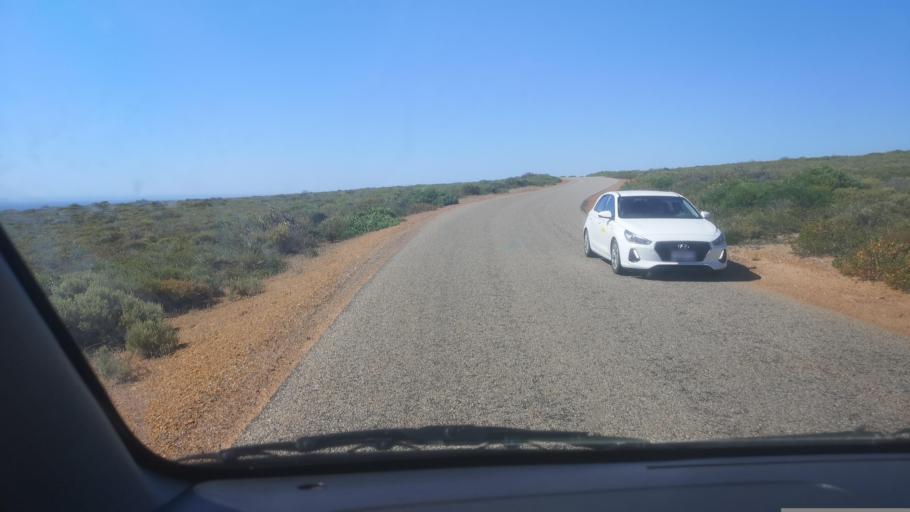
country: AU
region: Western Australia
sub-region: Northampton Shire
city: Kalbarri
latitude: -27.8193
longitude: 114.1166
